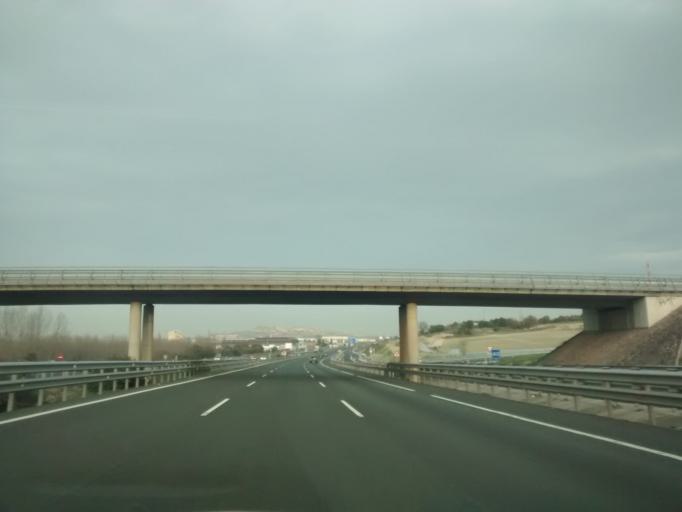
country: ES
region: Basque Country
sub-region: Provincia de Alava
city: Arminon
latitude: 42.8097
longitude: -2.7987
